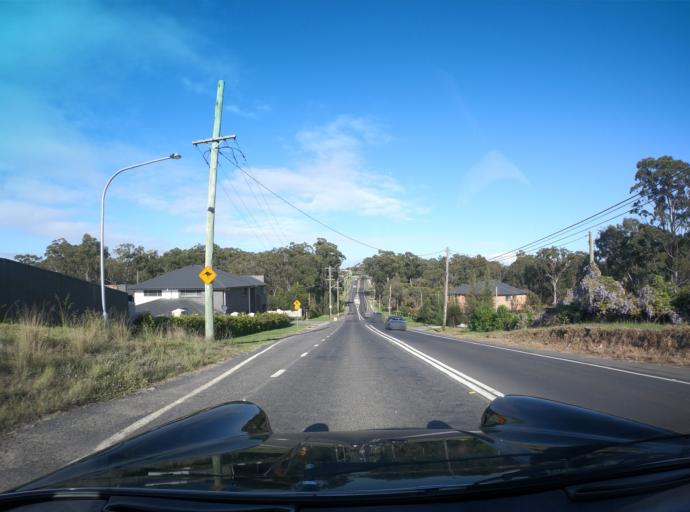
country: AU
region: New South Wales
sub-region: The Hills Shire
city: Beaumont Hills
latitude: -33.6875
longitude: 150.9452
